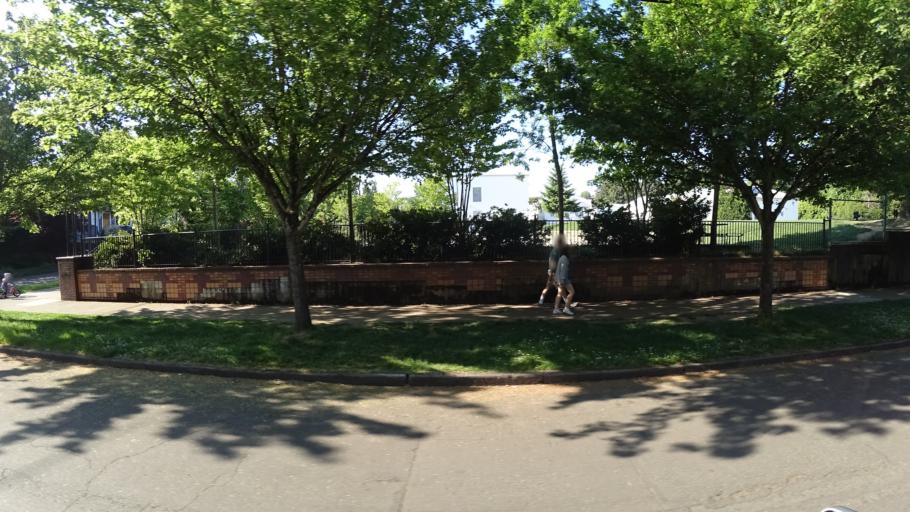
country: US
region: Oregon
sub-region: Multnomah County
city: Portland
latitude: 45.5467
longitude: -122.6378
